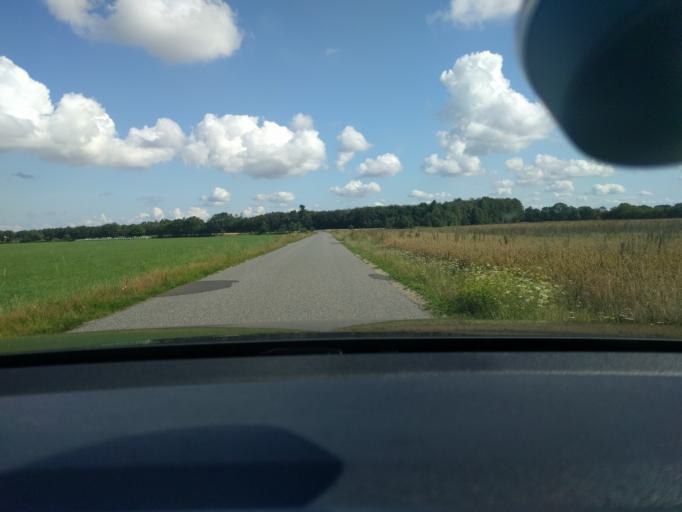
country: DK
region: Central Jutland
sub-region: Viborg Kommune
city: Viborg
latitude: 56.4332
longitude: 9.3133
